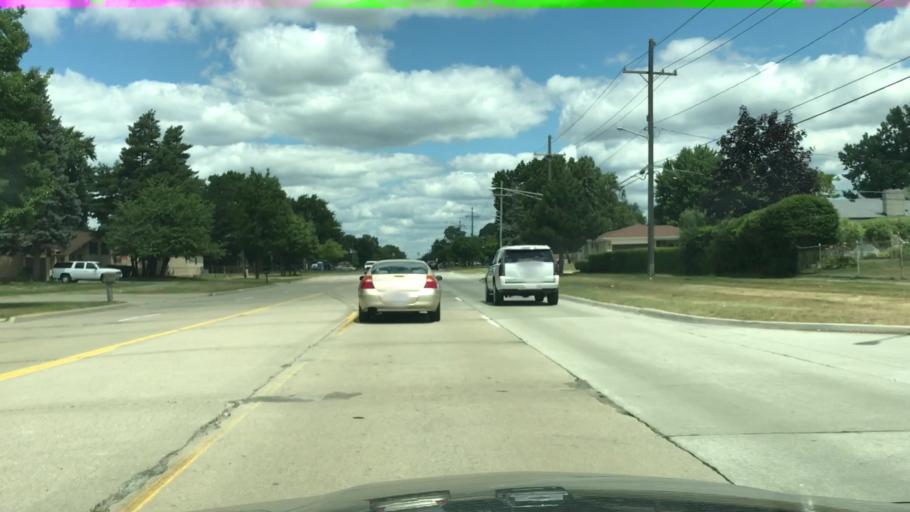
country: US
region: Michigan
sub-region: Macomb County
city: Sterling Heights
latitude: 42.5394
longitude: -83.0687
